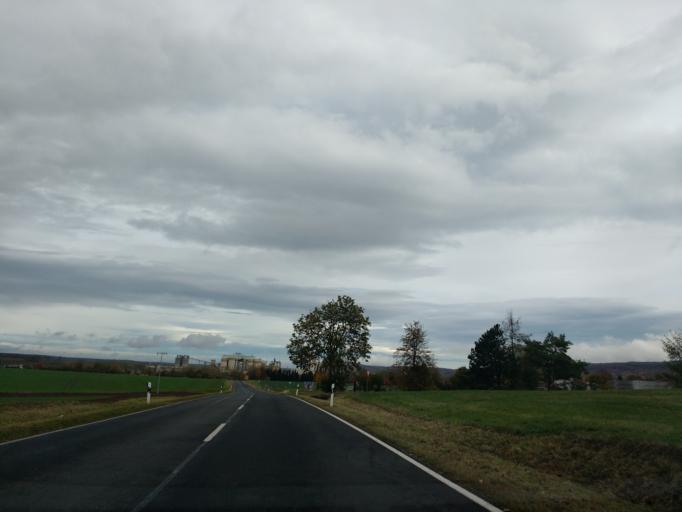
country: DE
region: Thuringia
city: Deuna
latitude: 51.3506
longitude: 10.4653
